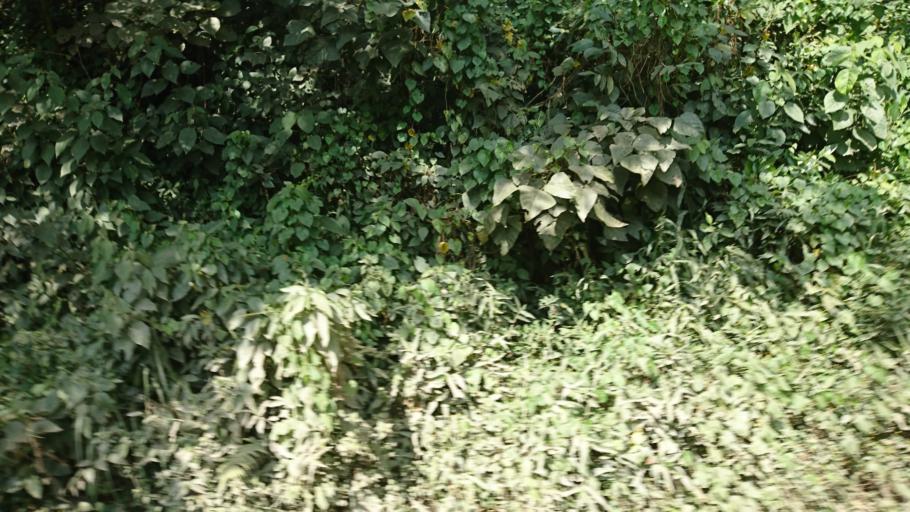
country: BO
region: La Paz
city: Coroico
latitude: -16.0875
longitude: -67.7851
